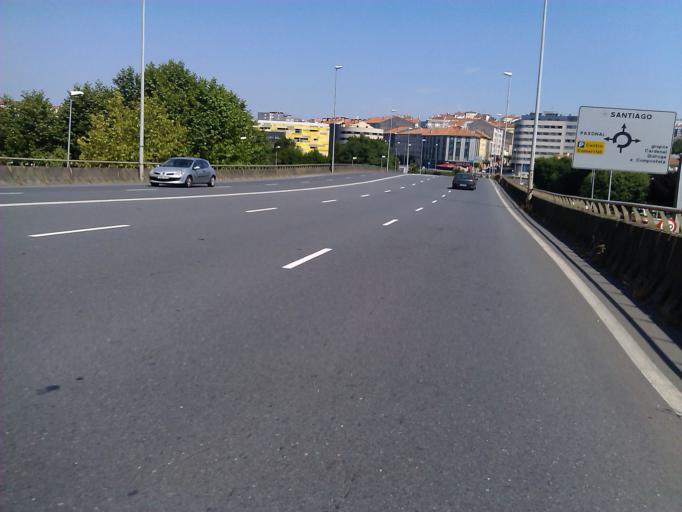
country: ES
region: Galicia
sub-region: Provincia da Coruna
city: Santiago de Compostela
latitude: 42.8652
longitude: -8.5434
